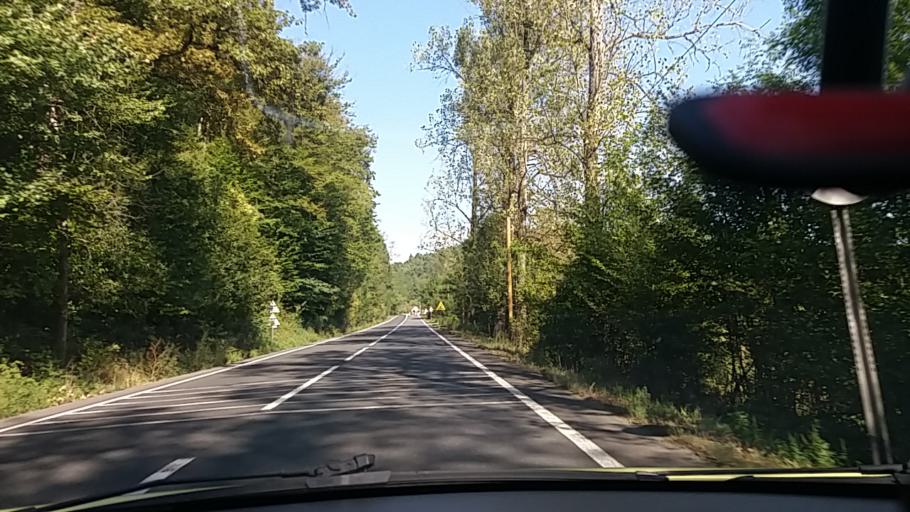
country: RO
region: Arad
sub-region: Comuna Petris
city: Petris
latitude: 46.0102
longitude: 22.3456
